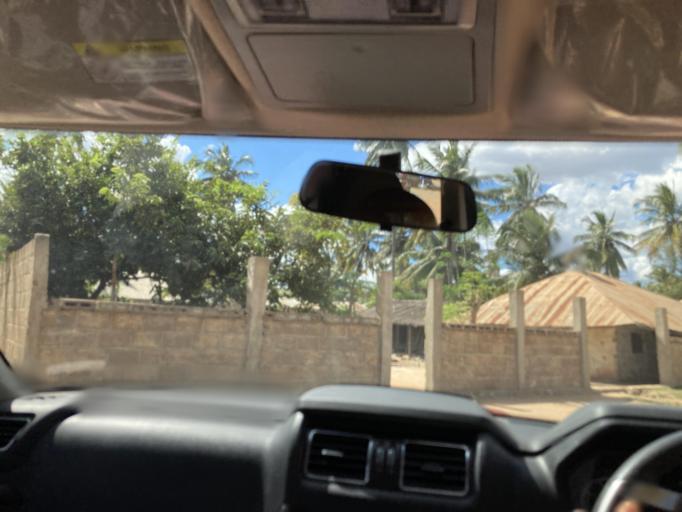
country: MZ
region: Cabo Delgado
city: Montepuez
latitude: -13.1342
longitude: 39.0054
